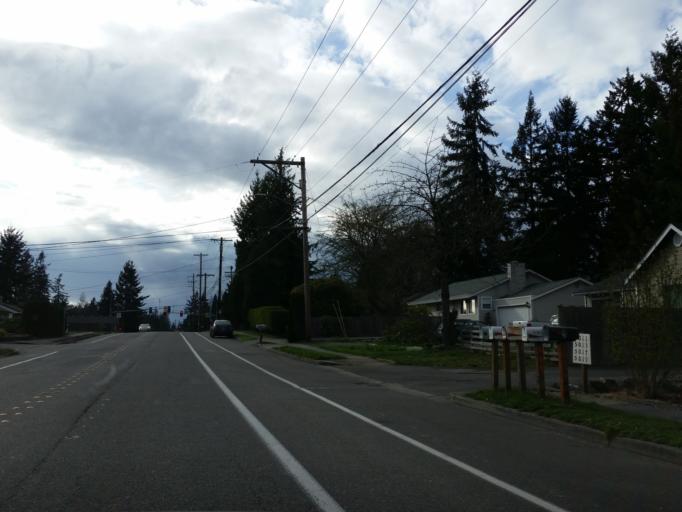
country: US
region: Washington
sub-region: Snohomish County
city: Lynnwood
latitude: 47.8283
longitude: -122.3009
